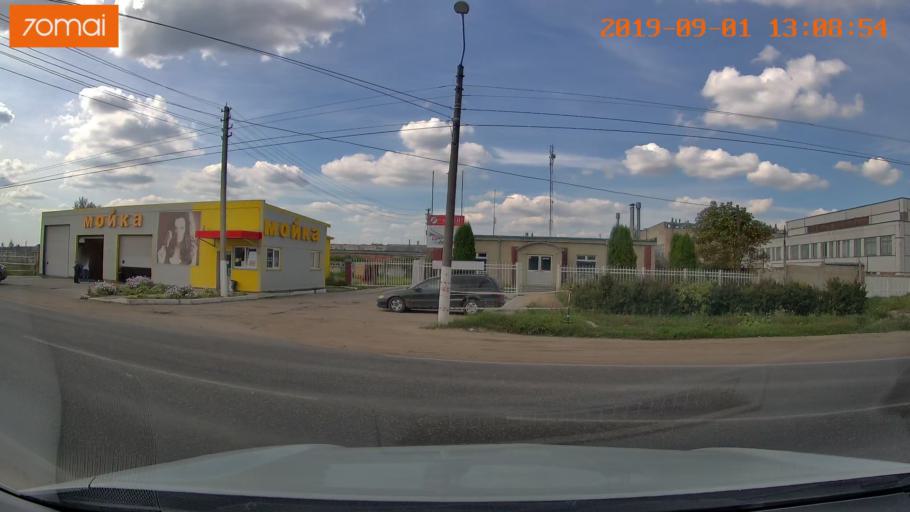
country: RU
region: Kaluga
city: Maloyaroslavets
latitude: 54.9998
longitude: 36.4394
